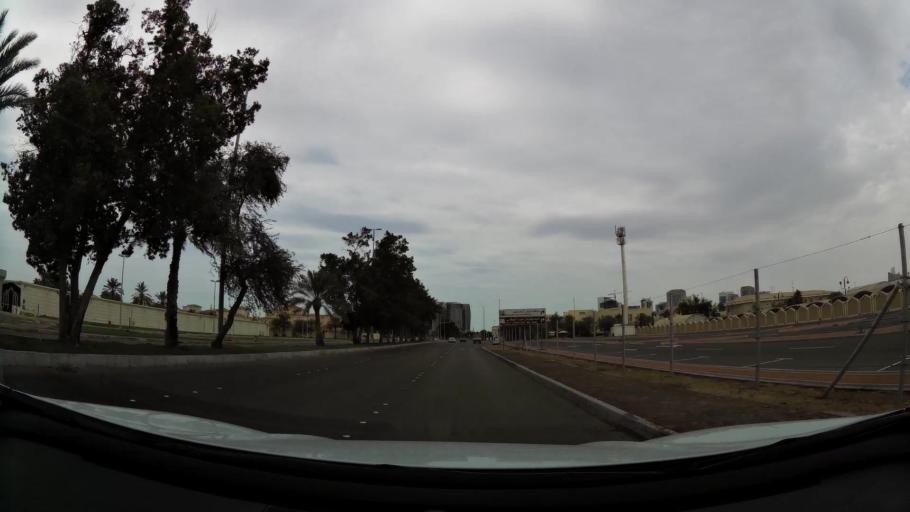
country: AE
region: Abu Dhabi
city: Abu Dhabi
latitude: 24.4218
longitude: 54.4278
